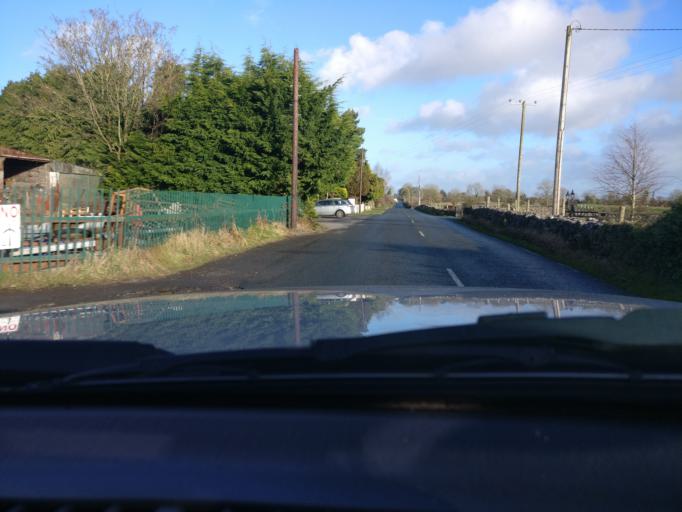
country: IE
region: Leinster
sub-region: An Iarmhi
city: Kilbeggan
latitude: 53.4578
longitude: -7.5132
